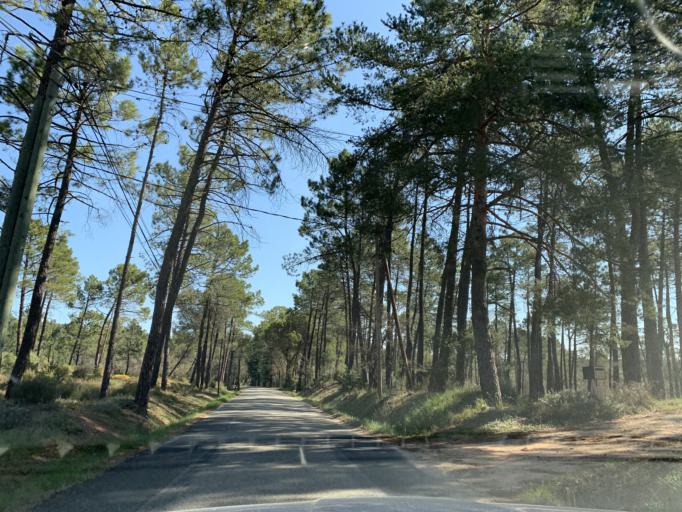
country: FR
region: Provence-Alpes-Cote d'Azur
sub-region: Departement du Vaucluse
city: Roussillon
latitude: 43.8887
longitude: 5.2750
